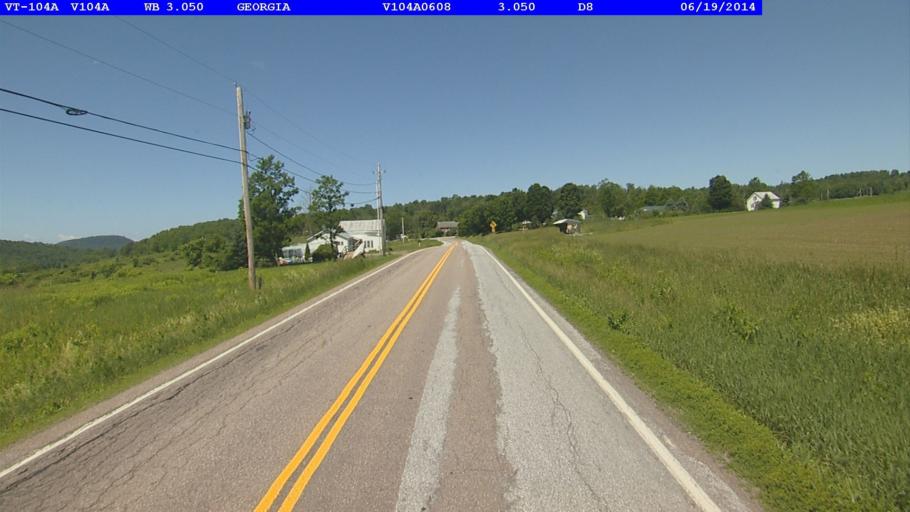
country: US
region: Vermont
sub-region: Chittenden County
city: Milton
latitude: 44.6832
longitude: -73.0567
